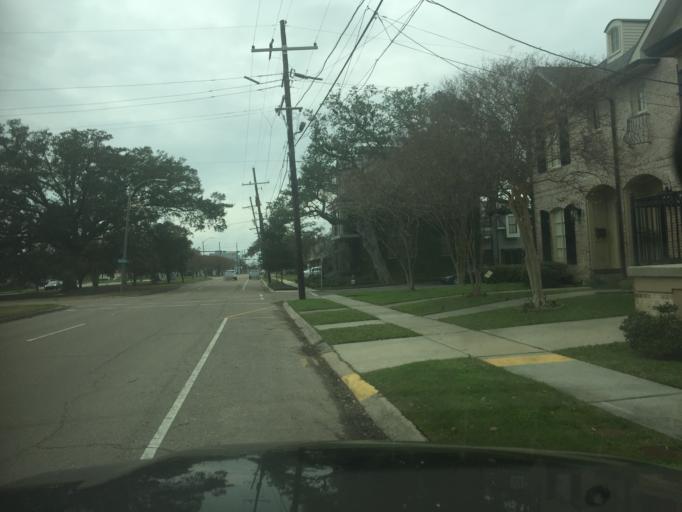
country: US
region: Louisiana
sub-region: Jefferson Parish
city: Metairie
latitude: 30.0053
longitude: -90.1132
